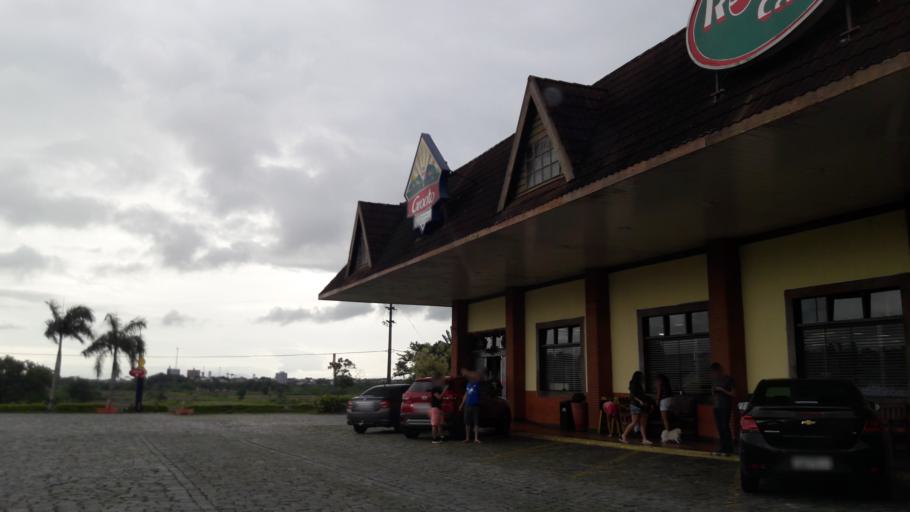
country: BR
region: Sao Paulo
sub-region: Registro
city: Registro
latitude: -24.4762
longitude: -47.8283
